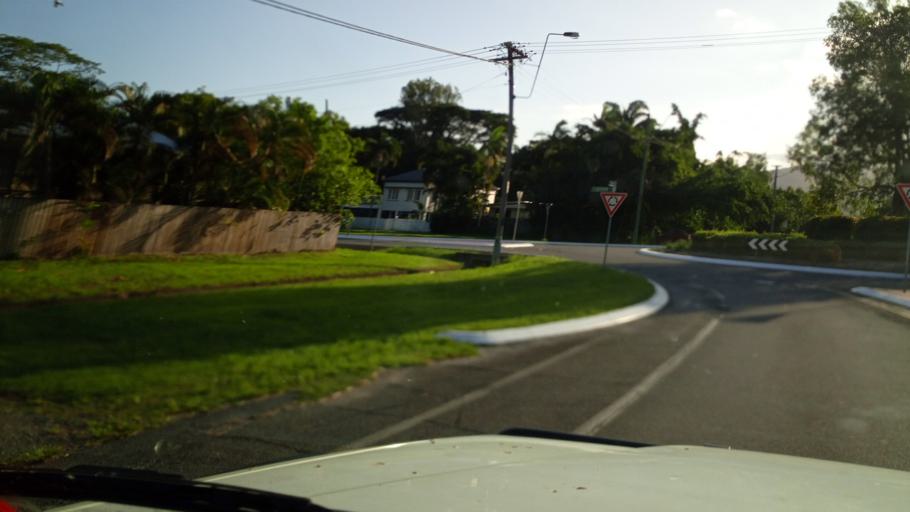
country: AU
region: Queensland
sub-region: Cairns
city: Cairns
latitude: -16.9183
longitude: 145.7592
